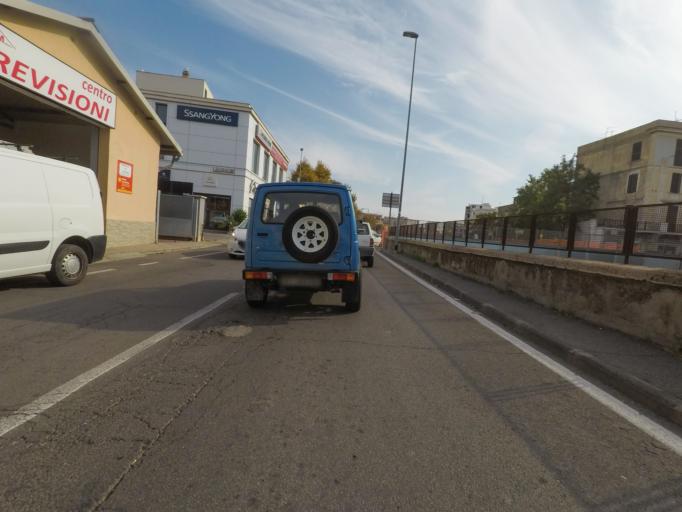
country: IT
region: Latium
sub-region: Citta metropolitana di Roma Capitale
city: Civitavecchia
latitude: 42.0955
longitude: 11.7944
